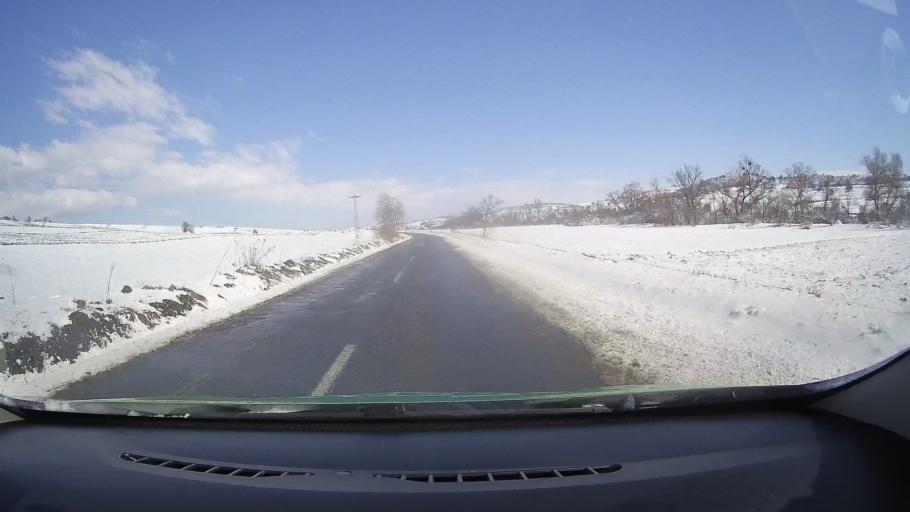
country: RO
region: Sibiu
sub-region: Comuna Vurpar
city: Vurpar
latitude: 45.8794
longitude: 24.3238
